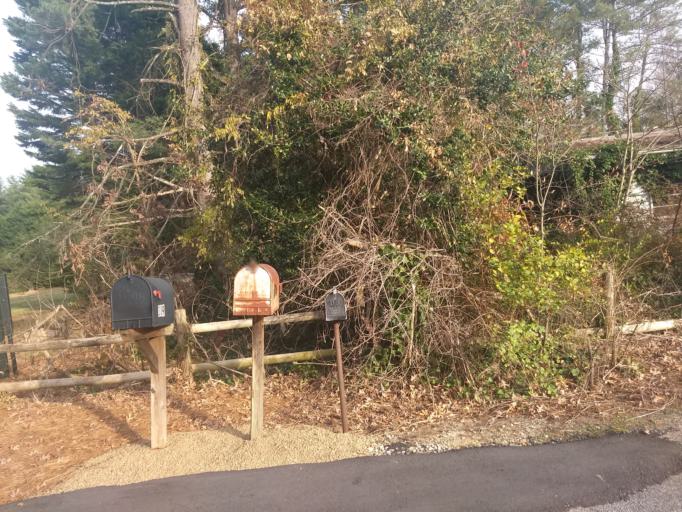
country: US
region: South Carolina
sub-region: Greenville County
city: Wade Hampton
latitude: 34.8735
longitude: -82.3521
